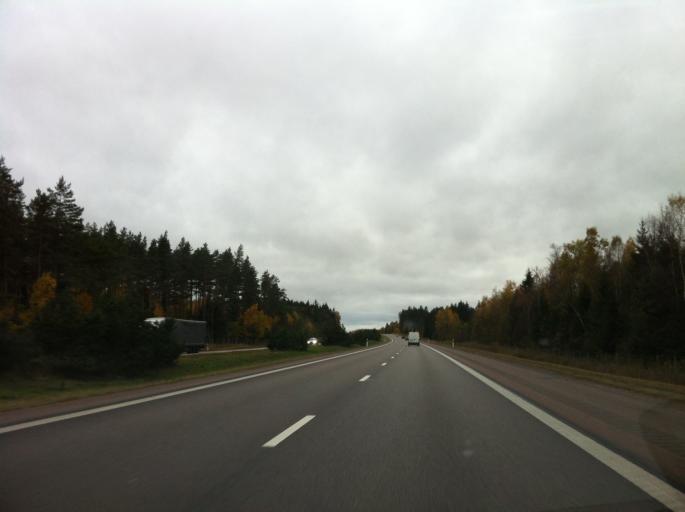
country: SE
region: OEstergoetland
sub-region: Mjolby Kommun
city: Mjolby
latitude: 58.3212
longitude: 15.0664
